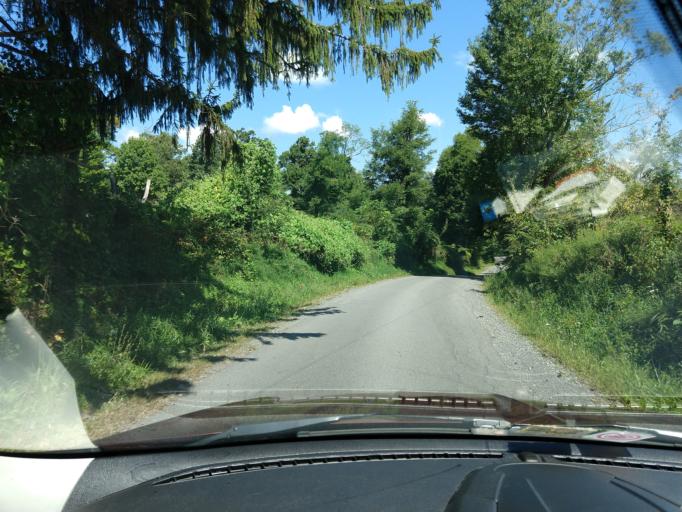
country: US
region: West Virginia
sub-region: Nicholas County
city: Craigsville
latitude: 38.2607
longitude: -80.6935
